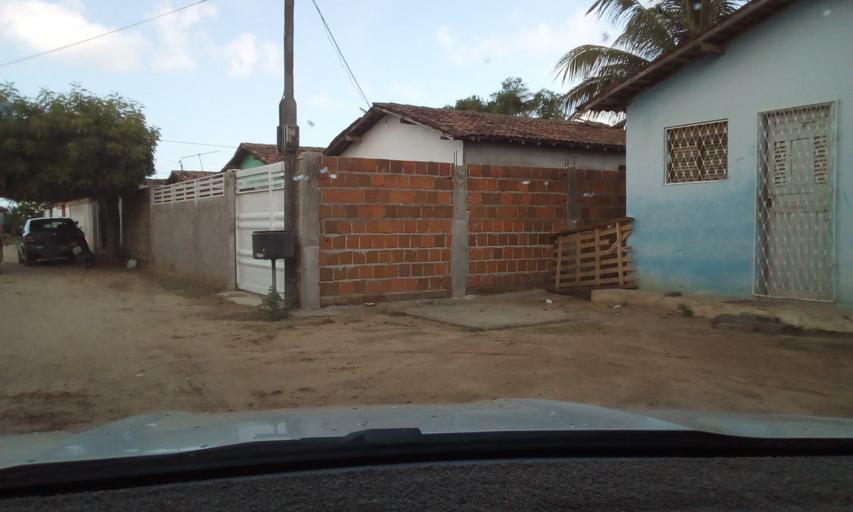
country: BR
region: Paraiba
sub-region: Joao Pessoa
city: Joao Pessoa
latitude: -7.1693
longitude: -34.8235
